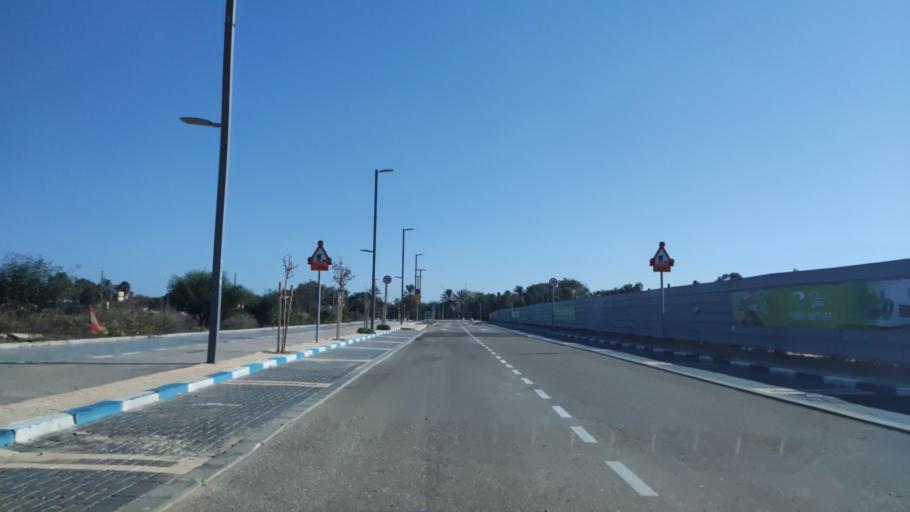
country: IL
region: Tel Aviv
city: Herzliya Pituah
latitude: 32.1560
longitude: 34.8049
